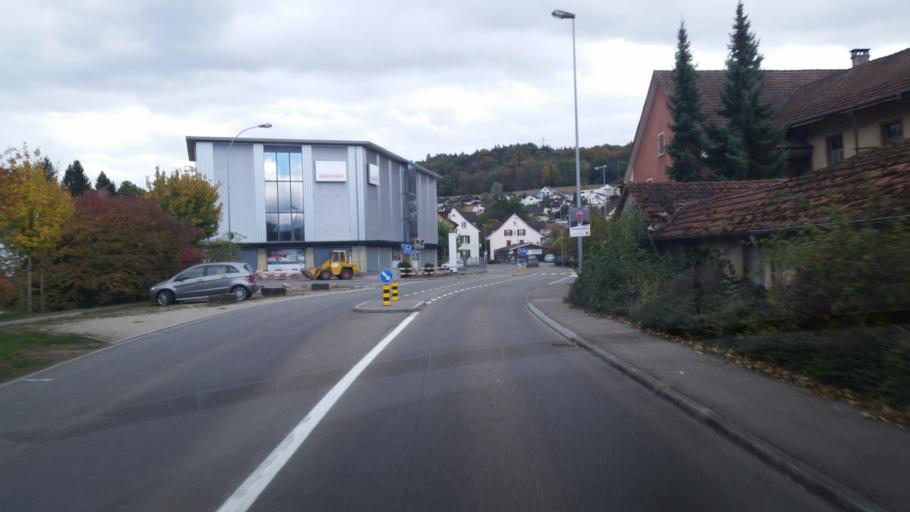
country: CH
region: Aargau
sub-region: Bezirk Zurzach
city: Oberendingen
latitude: 47.5387
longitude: 8.2902
